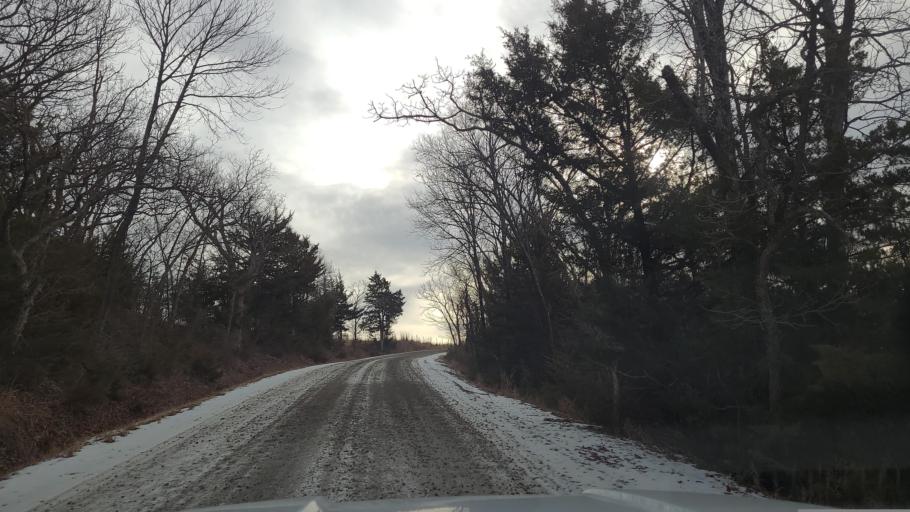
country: US
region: Kansas
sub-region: Shawnee County
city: Topeka
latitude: 39.0459
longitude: -95.4725
